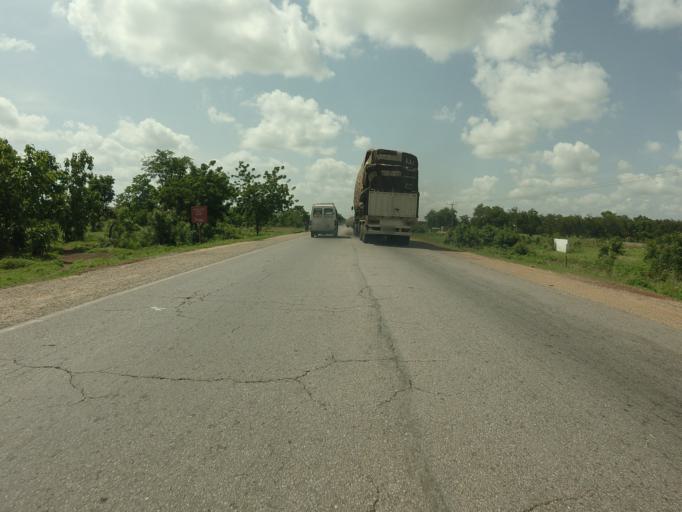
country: GH
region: Northern
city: Savelugu
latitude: 9.5629
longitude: -0.8361
